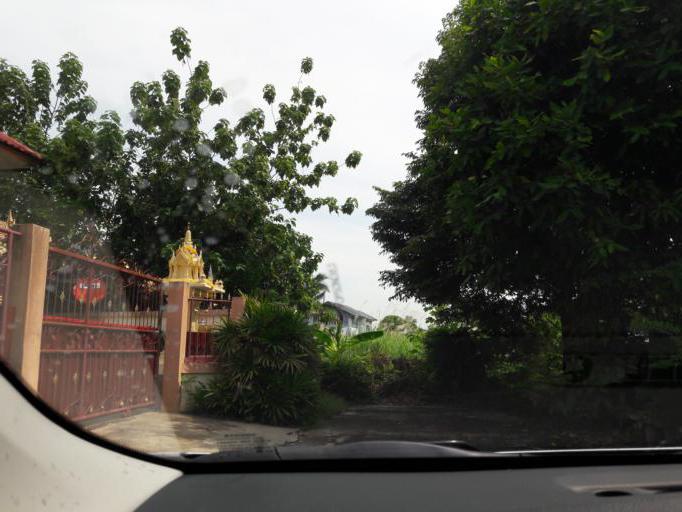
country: TH
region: Ang Thong
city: Ang Thong
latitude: 14.5743
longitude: 100.4569
